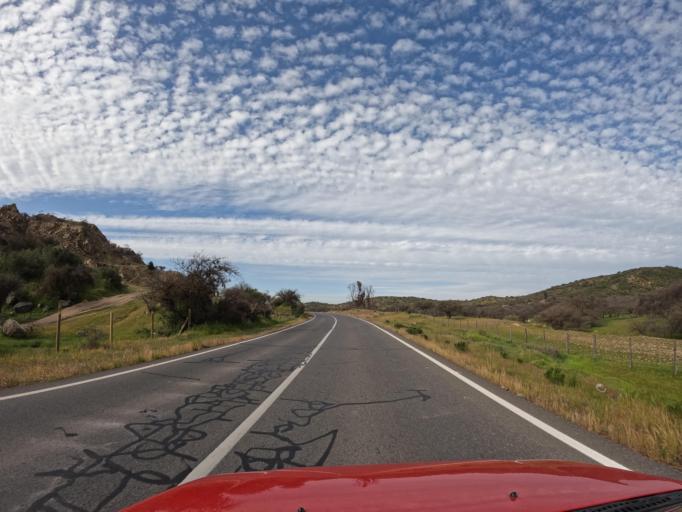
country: CL
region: O'Higgins
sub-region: Provincia de Colchagua
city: Santa Cruz
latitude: -34.3127
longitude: -71.7391
